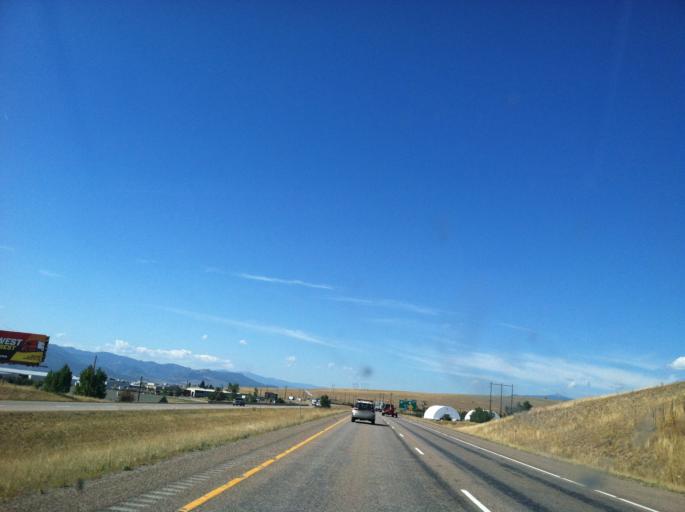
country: US
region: Montana
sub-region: Missoula County
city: Orchard Homes
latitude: 46.9343
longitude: -114.0900
